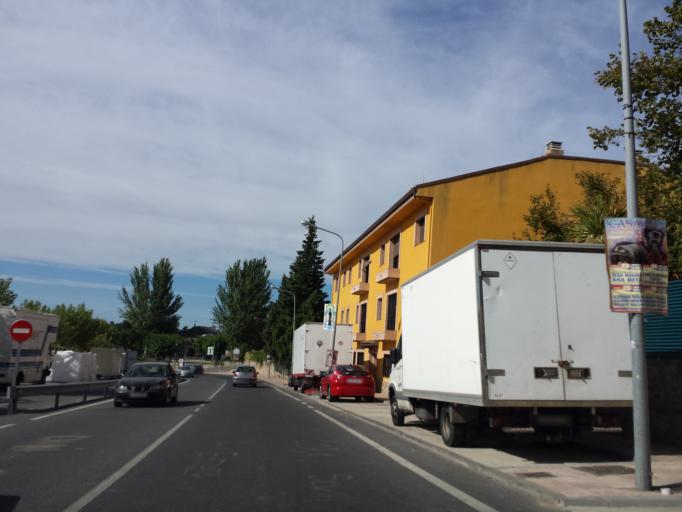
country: ES
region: Castille and Leon
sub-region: Provincia de Avila
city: Piedralaves
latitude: 40.3154
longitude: -4.7019
